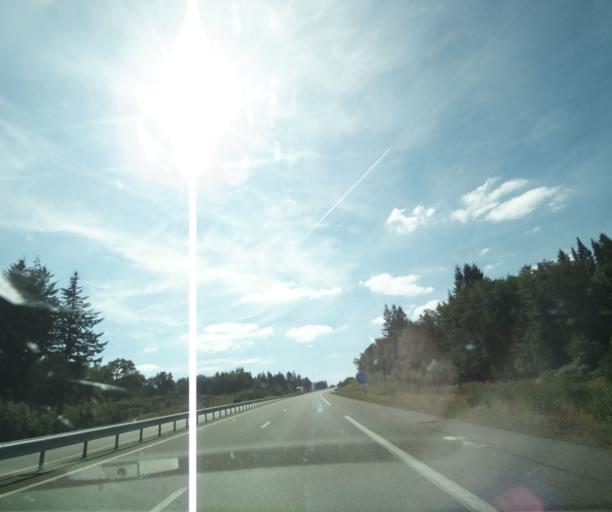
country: FR
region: Auvergne
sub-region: Departement du Puy-de-Dome
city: Gelles
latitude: 45.7398
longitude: 2.7095
